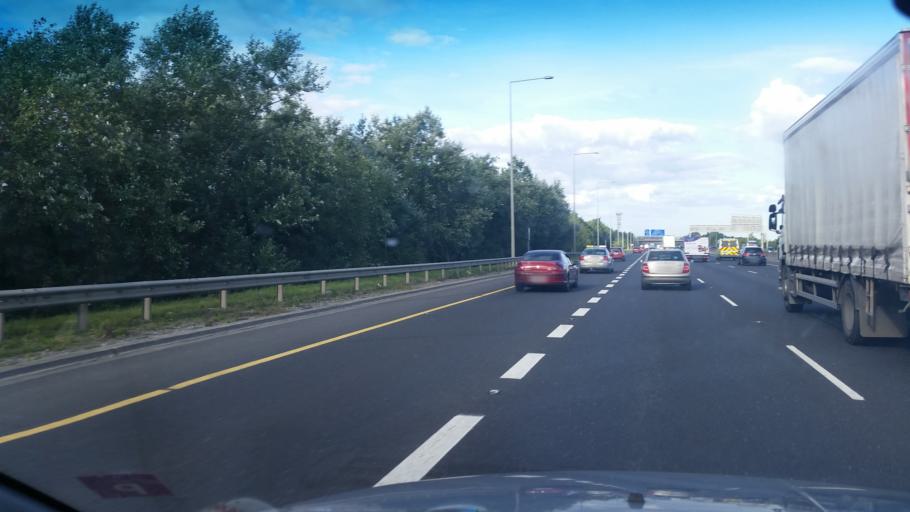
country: IE
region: Leinster
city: Castleknock
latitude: 53.3942
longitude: -6.3398
